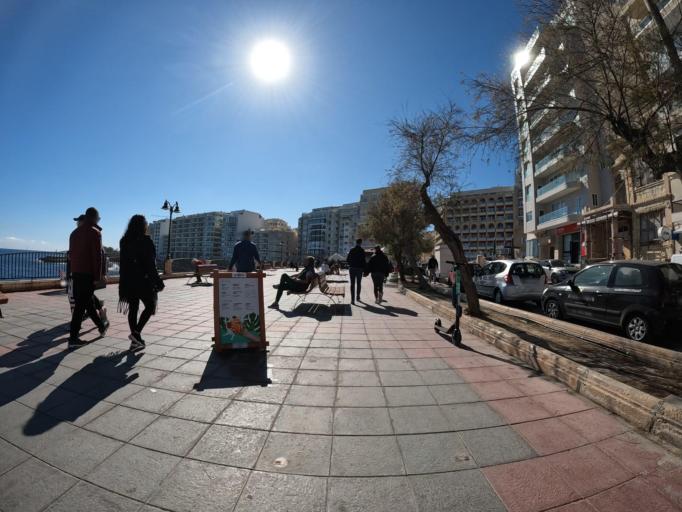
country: MT
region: Tas-Sliema
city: Sliema
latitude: 35.9127
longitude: 14.5068
